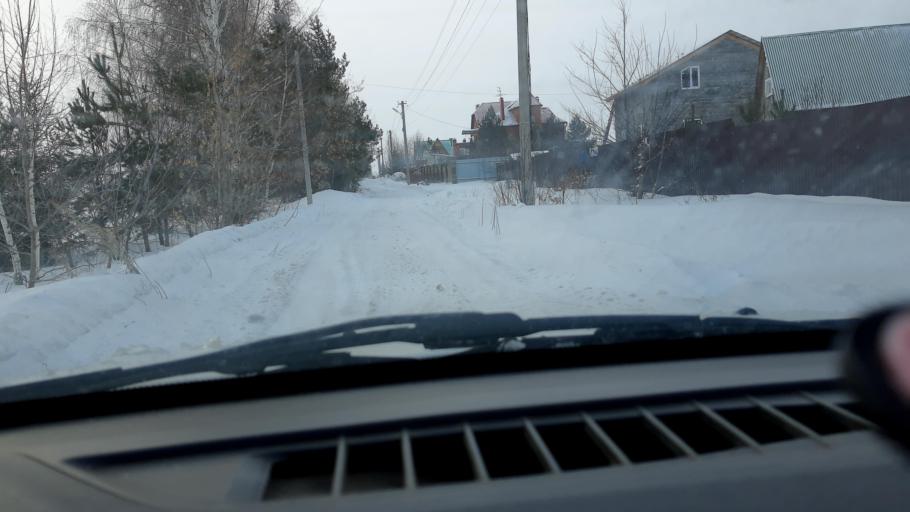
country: RU
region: Bashkortostan
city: Avdon
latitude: 54.5999
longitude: 55.7983
